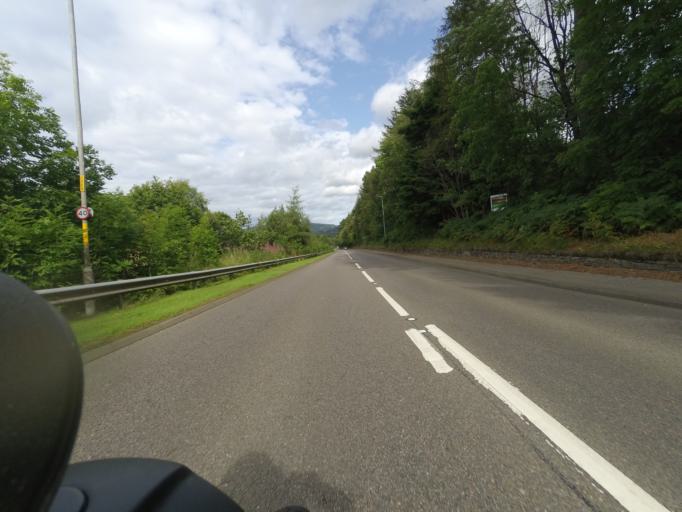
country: GB
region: Scotland
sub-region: Moray
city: Rothes
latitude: 57.4650
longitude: -3.2372
